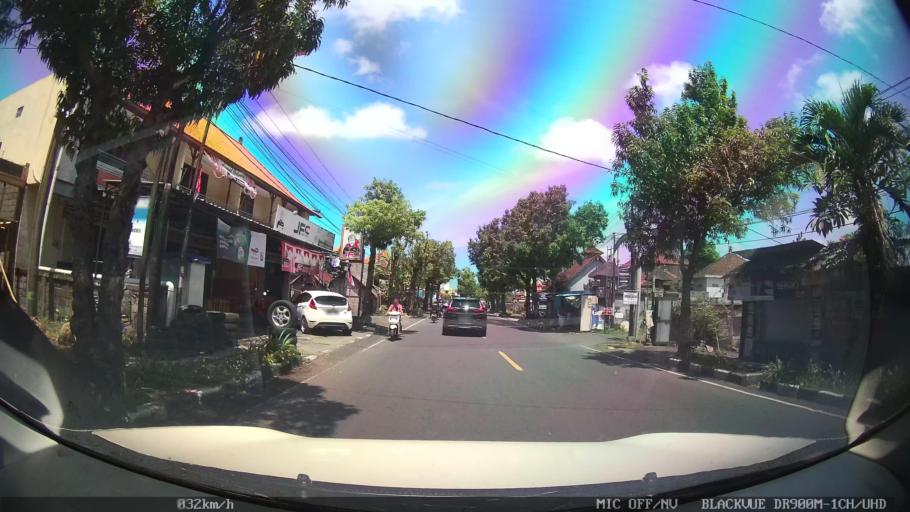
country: ID
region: Bali
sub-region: Kabupaten Gianyar
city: Ubud
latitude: -8.5511
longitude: 115.3031
